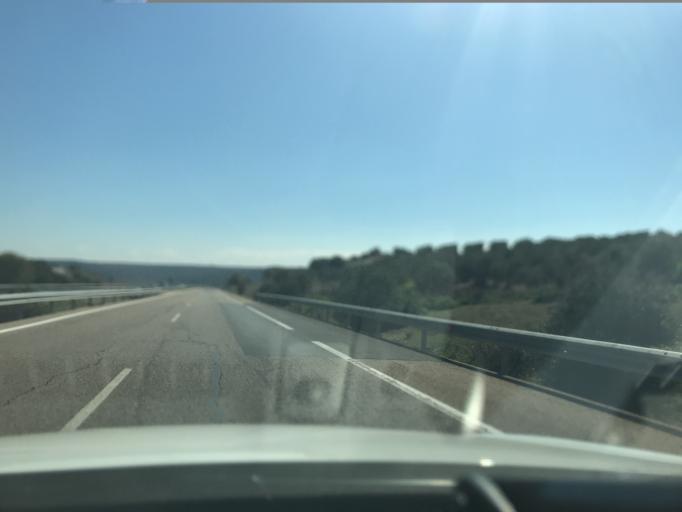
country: ES
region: Andalusia
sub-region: Provincia de Jaen
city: Marmolejo
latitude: 38.0071
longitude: -4.2150
